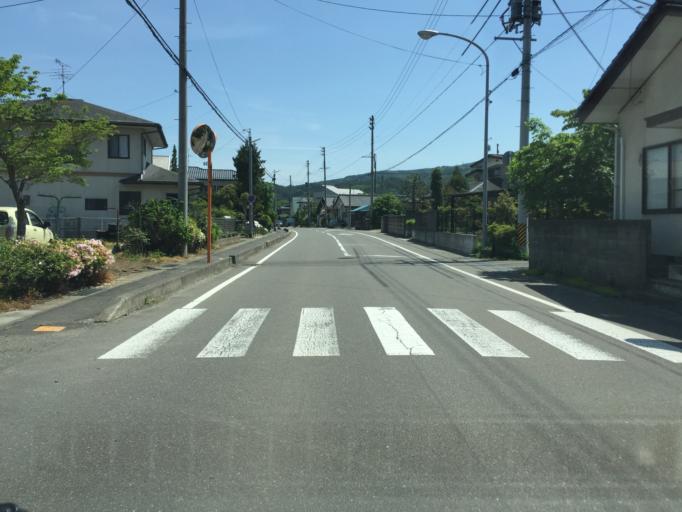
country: JP
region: Fukushima
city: Fukushima-shi
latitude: 37.7154
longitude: 140.3808
